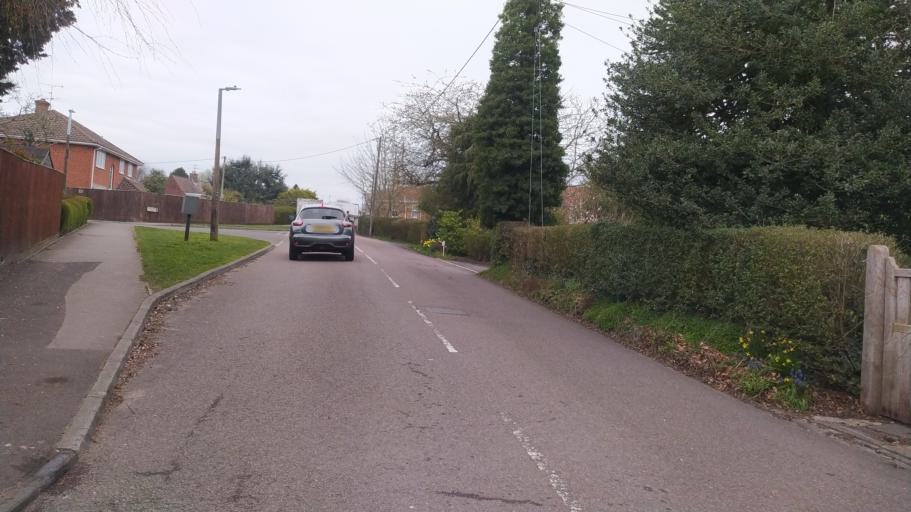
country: GB
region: England
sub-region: Wiltshire
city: Devizes
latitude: 51.3437
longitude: -1.9883
